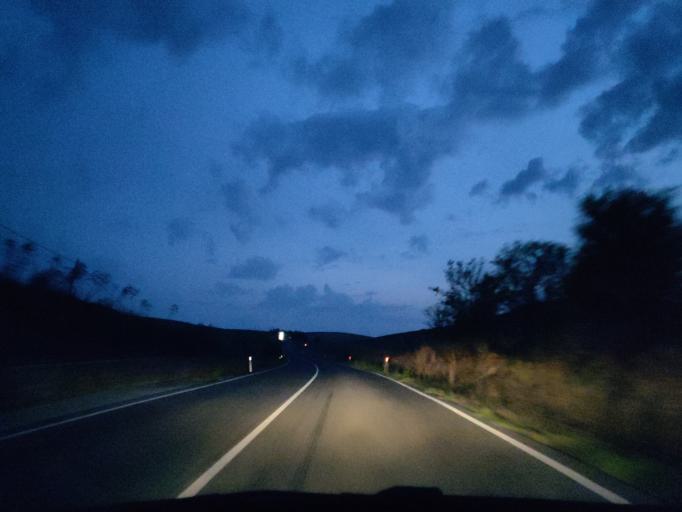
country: IT
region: Latium
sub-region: Provincia di Viterbo
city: Tarquinia
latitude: 42.2504
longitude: 11.8111
